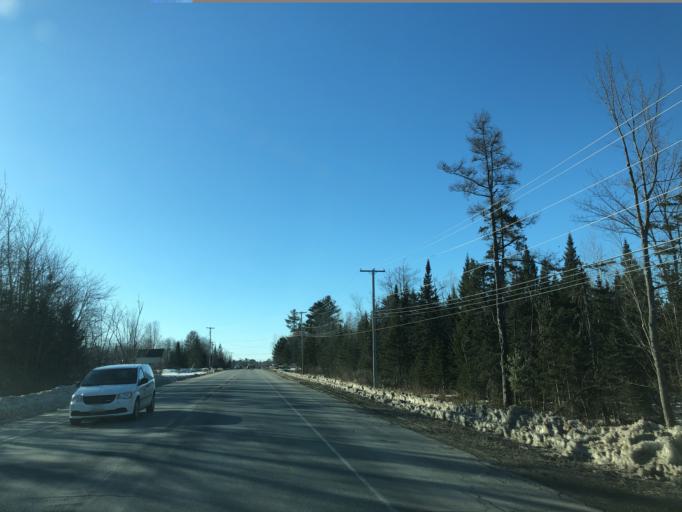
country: US
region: Maine
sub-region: Penobscot County
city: Kenduskeag
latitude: 44.9139
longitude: -68.9104
